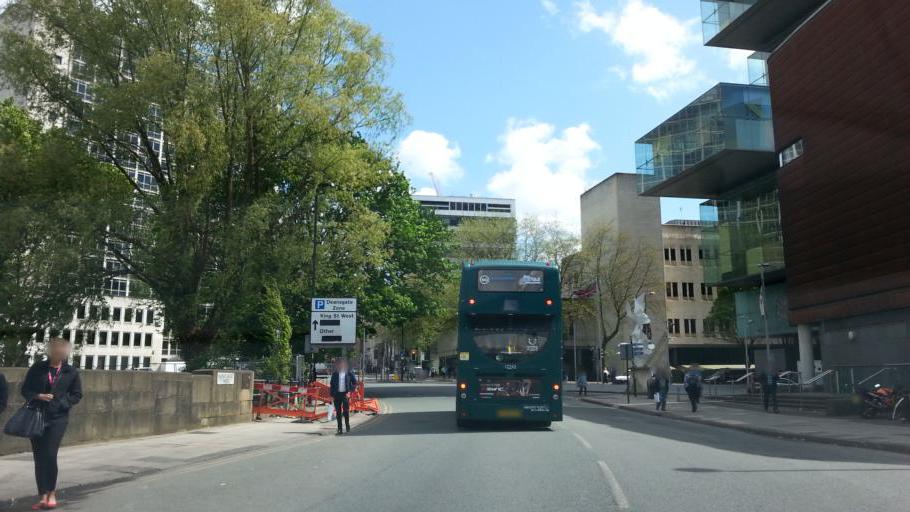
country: GB
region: England
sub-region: Manchester
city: Manchester
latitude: 53.4814
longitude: -2.2533
